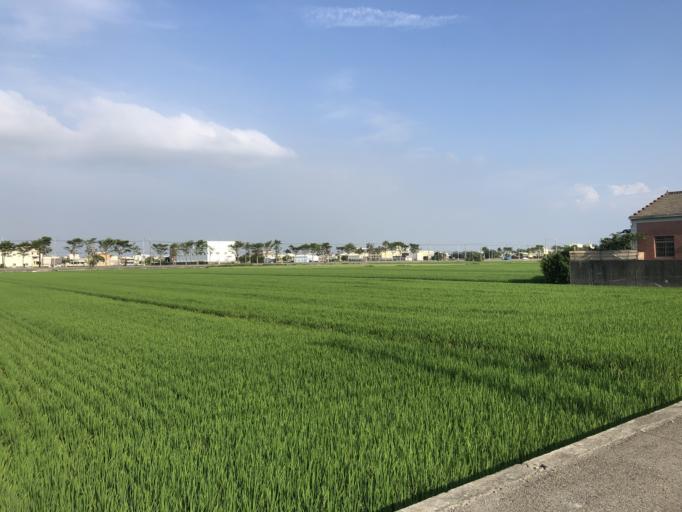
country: TW
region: Taiwan
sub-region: Changhua
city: Chang-hua
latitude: 24.0540
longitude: 120.4671
